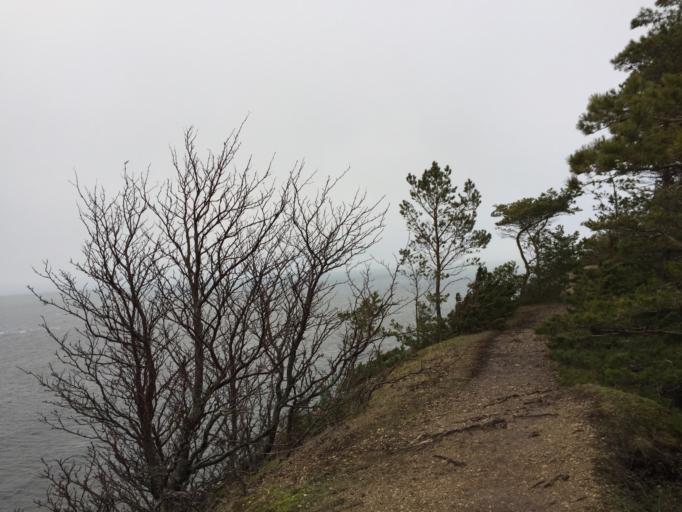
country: EE
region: Saare
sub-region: Kuressaare linn
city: Kuressaare
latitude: 58.5685
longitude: 22.2860
